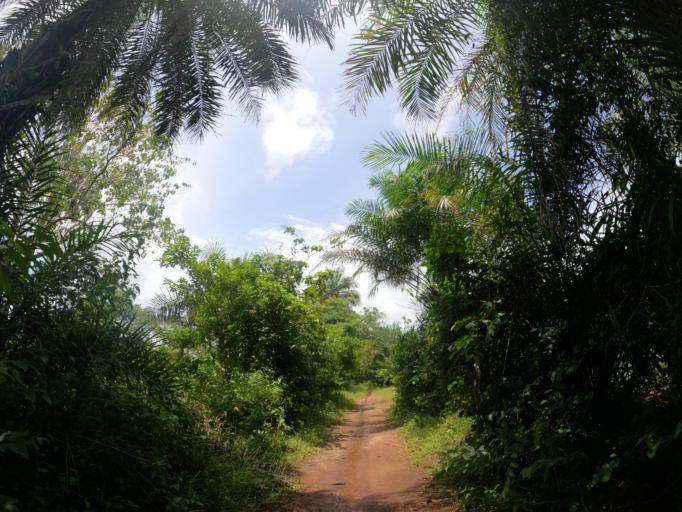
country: SL
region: Northern Province
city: Binkolo
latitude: 9.1395
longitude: -12.2386
